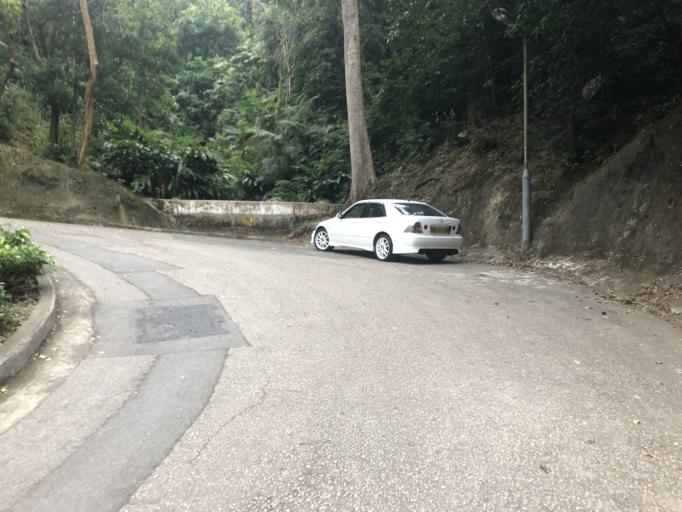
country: HK
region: Wanchai
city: Wan Chai
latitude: 22.2821
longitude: 114.2117
